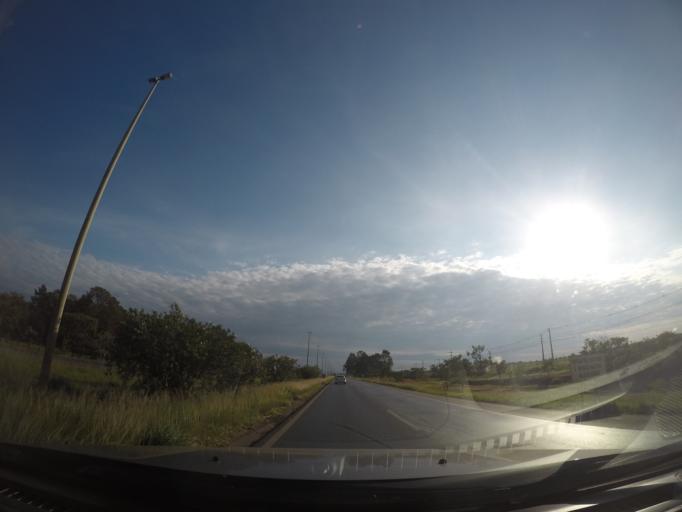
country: BR
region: Federal District
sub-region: Brasilia
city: Brasilia
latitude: -15.6394
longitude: -47.7505
